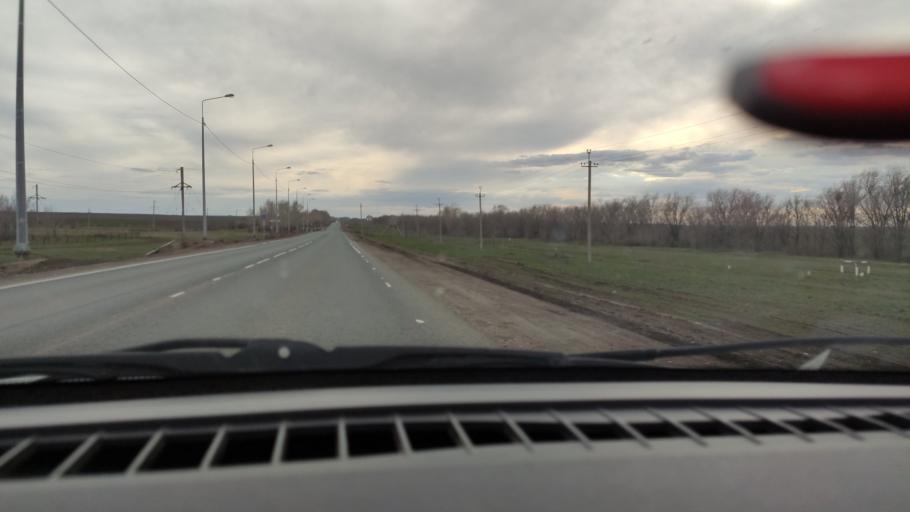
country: RU
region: Orenburg
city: Sakmara
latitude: 52.3284
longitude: 55.4974
